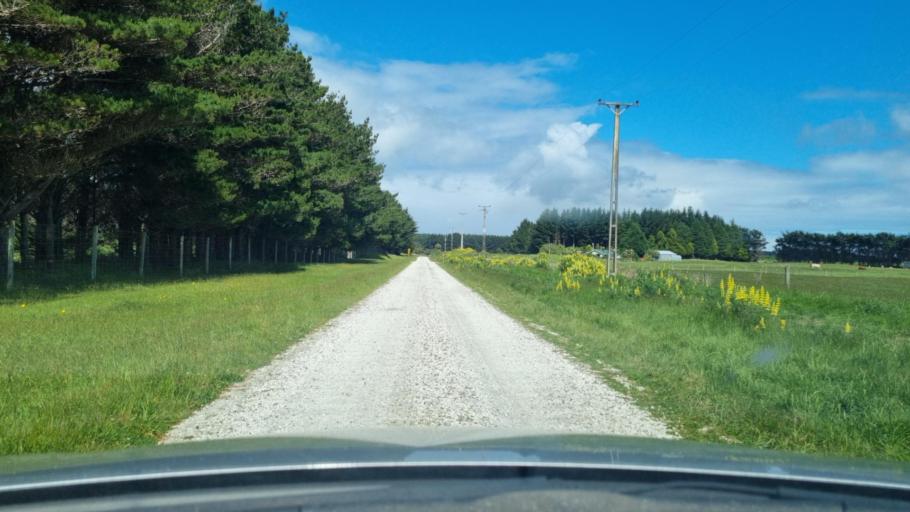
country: NZ
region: Southland
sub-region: Invercargill City
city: Invercargill
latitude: -46.4563
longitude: 168.2733
